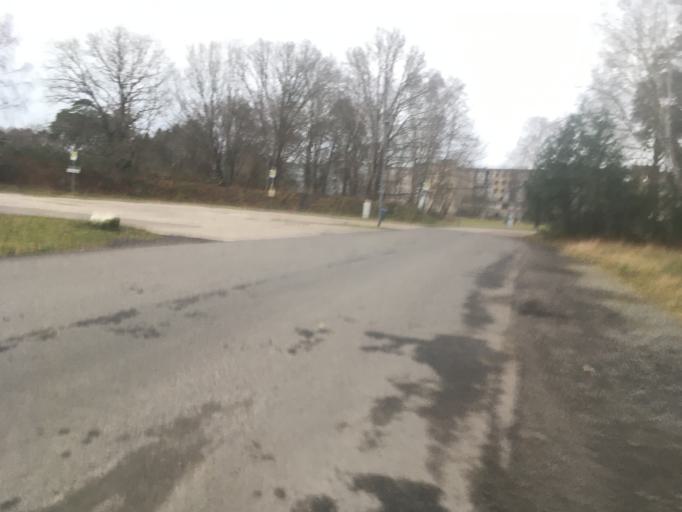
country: DE
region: Mecklenburg-Vorpommern
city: Ostseebad Binz
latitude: 54.4489
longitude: 13.5677
